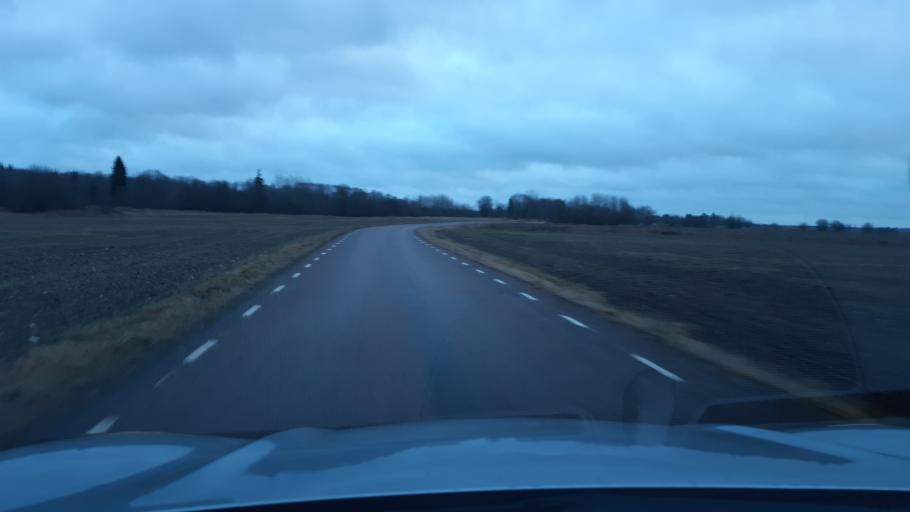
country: EE
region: Raplamaa
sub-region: Rapla vald
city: Rapla
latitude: 59.0091
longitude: 24.7077
